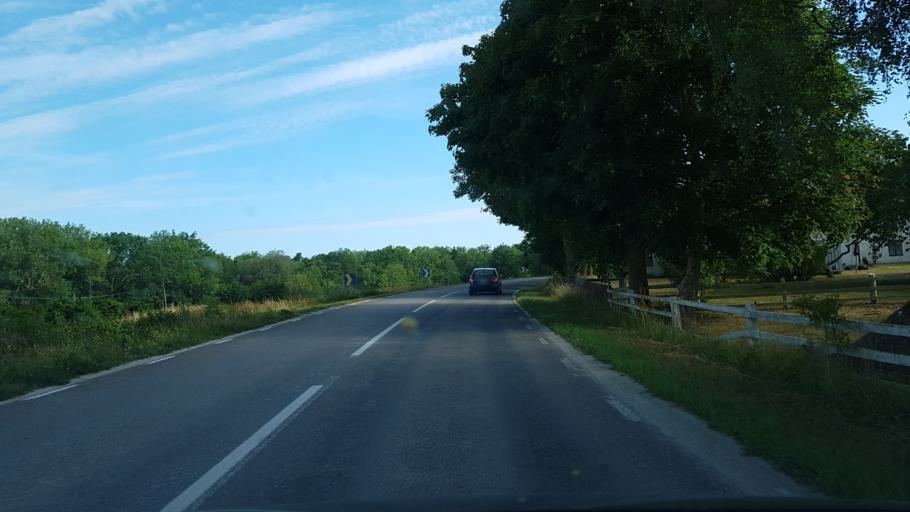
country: SE
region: Gotland
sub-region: Gotland
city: Visby
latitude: 57.7603
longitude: 18.4269
